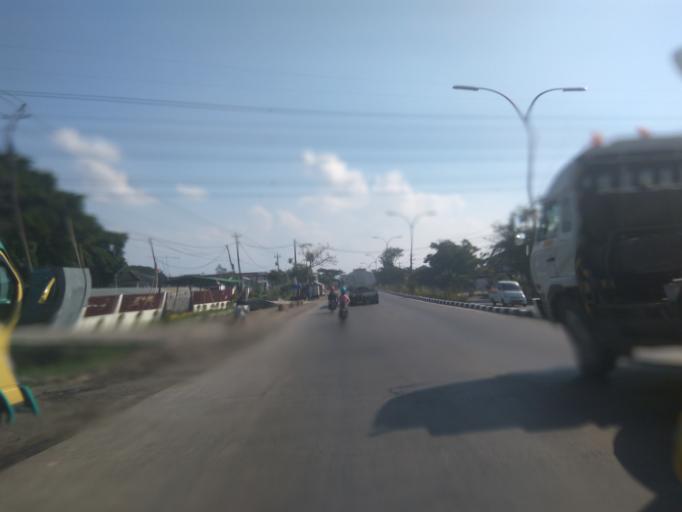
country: ID
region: Central Java
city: Semarang
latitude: -6.9498
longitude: 110.4852
